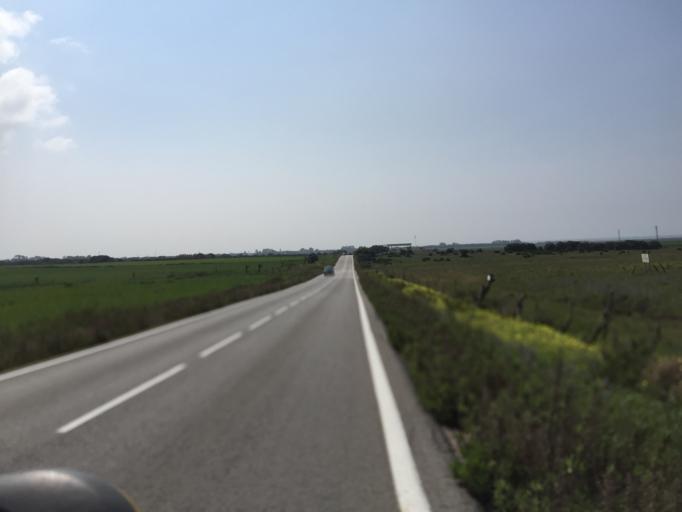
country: ES
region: Andalusia
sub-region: Provincia de Cadiz
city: Conil de la Frontera
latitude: 36.2266
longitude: -6.0398
